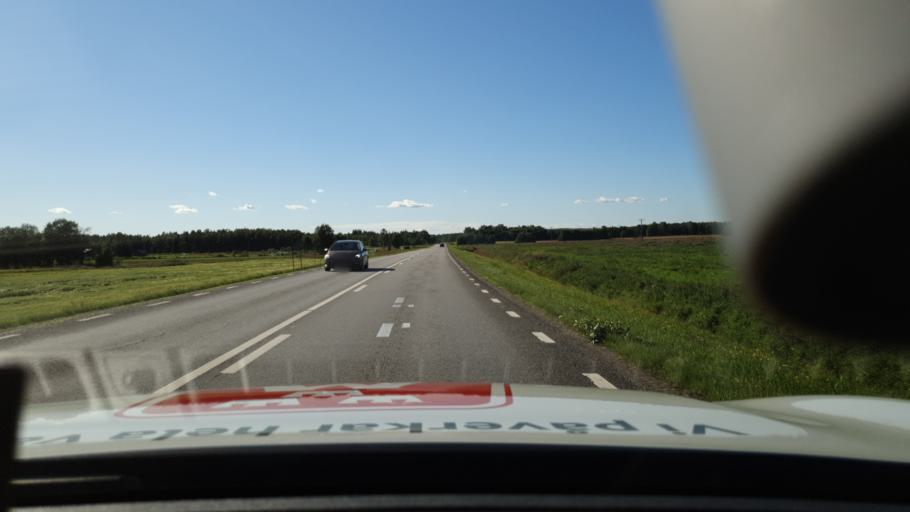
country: SE
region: Norrbotten
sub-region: Pitea Kommun
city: Rosvik
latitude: 65.5713
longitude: 21.7548
